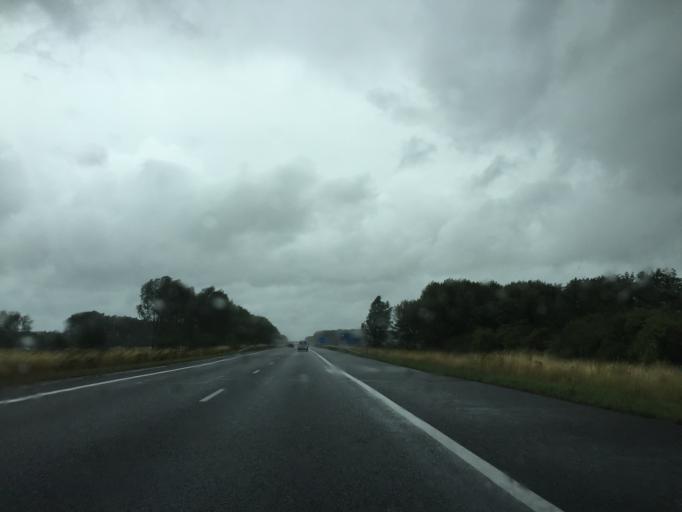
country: NL
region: Flevoland
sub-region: Gemeente Almere
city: Almere Stad
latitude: 52.3927
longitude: 5.3300
